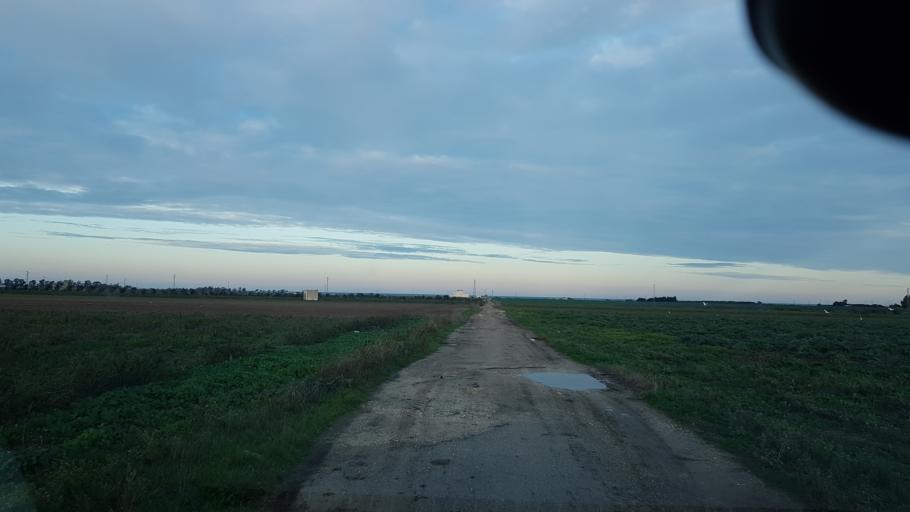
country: IT
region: Apulia
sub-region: Provincia di Brindisi
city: La Rosa
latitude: 40.5990
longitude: 17.9956
